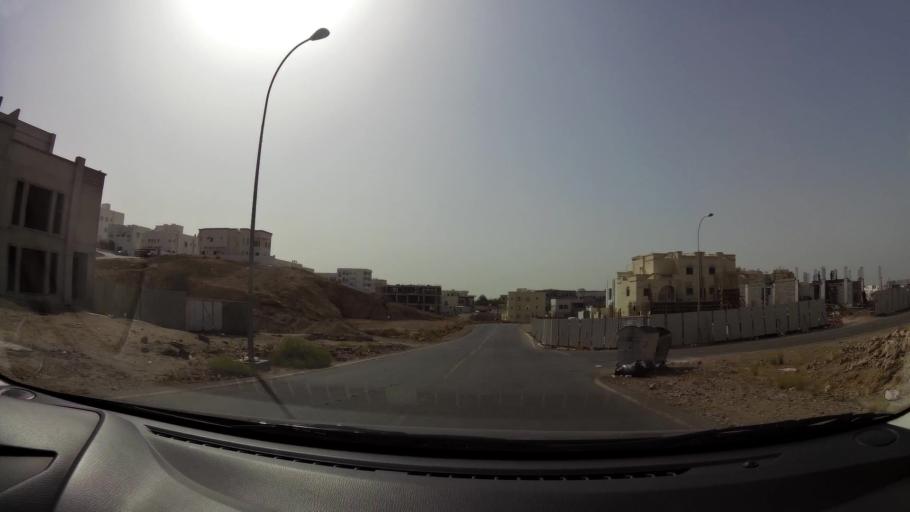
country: OM
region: Muhafazat Masqat
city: Bawshar
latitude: 23.5548
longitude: 58.3499
